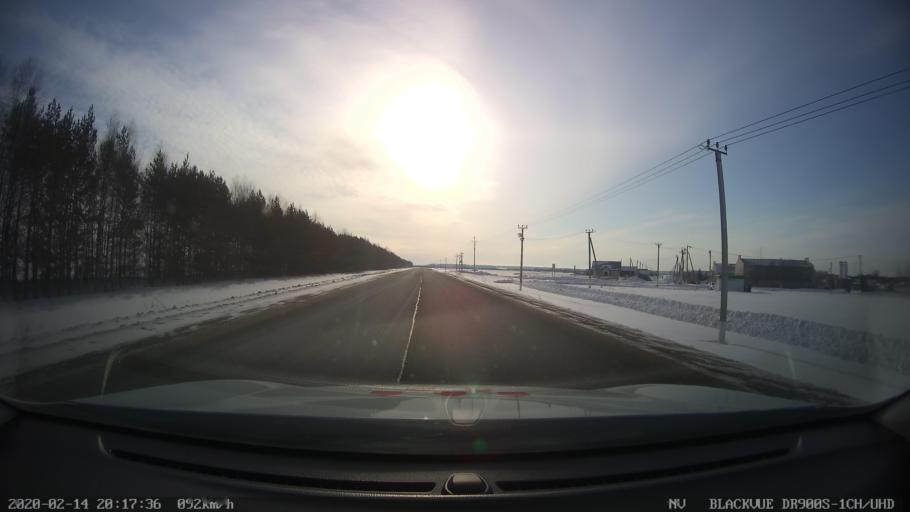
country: RU
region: Tatarstan
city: Verkhniy Uslon
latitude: 55.5976
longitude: 48.8787
